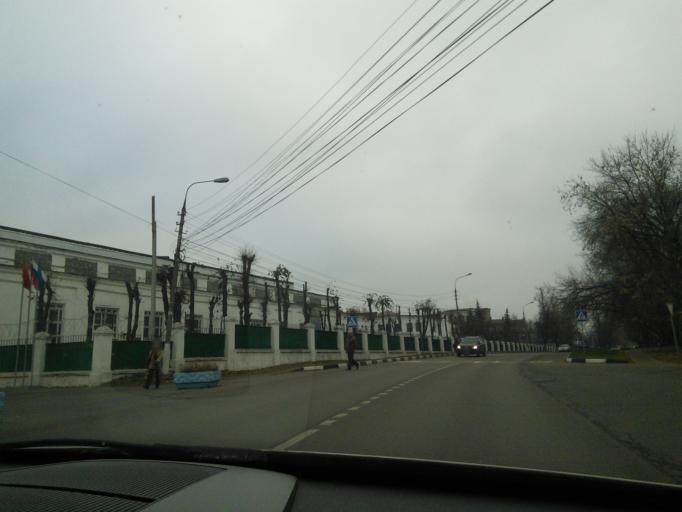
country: RU
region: Moskovskaya
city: Udel'naya
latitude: 55.6363
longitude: 38.0102
